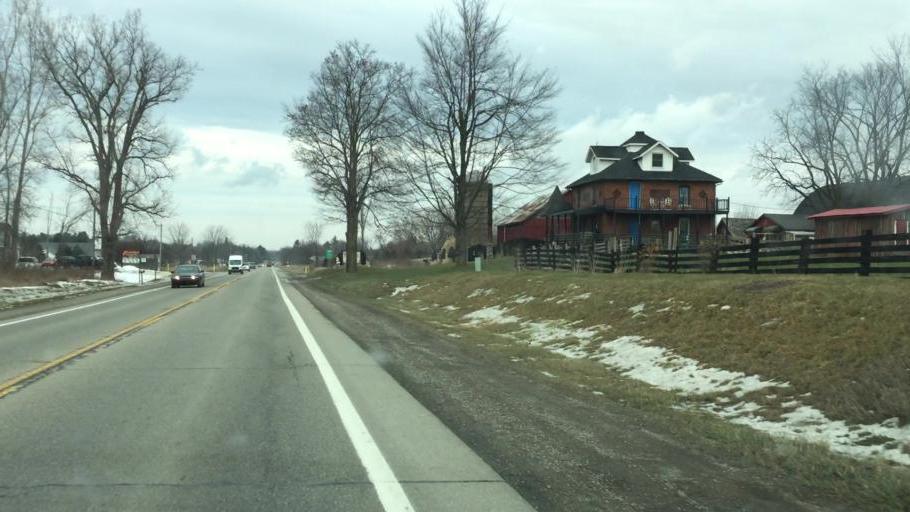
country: US
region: Michigan
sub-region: Lapeer County
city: Barnes Lake-Millers Lake
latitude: 43.1910
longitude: -83.3125
